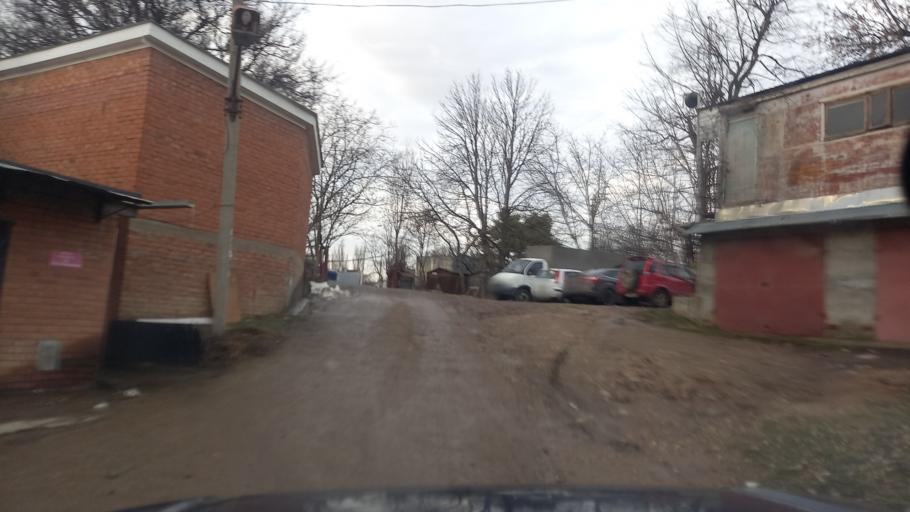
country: RU
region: Krasnodarskiy
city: Pashkovskiy
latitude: 45.0194
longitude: 39.0435
